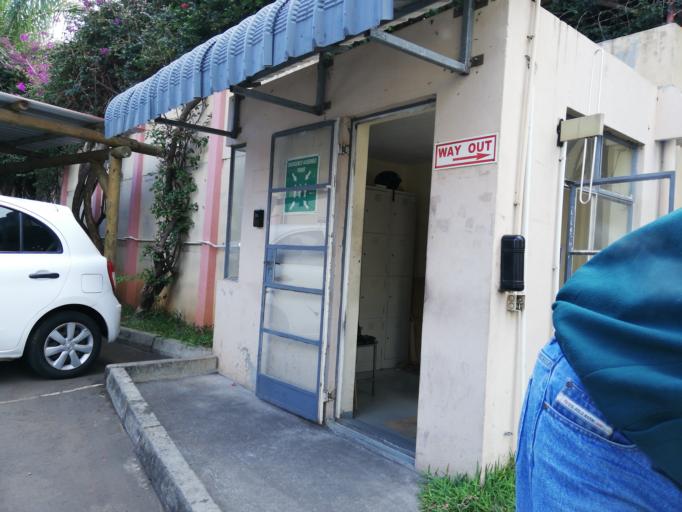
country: MU
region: Black River
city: Petite Riviere
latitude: -20.1903
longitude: 57.4652
